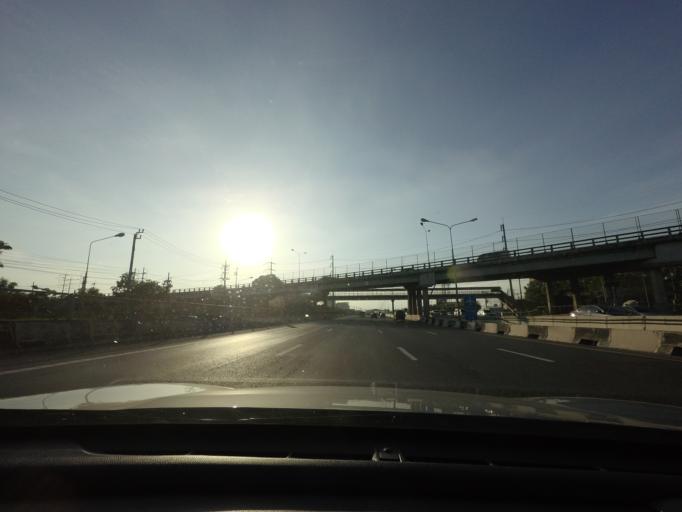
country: TH
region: Bangkok
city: Lat Krabang
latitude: 13.7322
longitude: 100.7848
